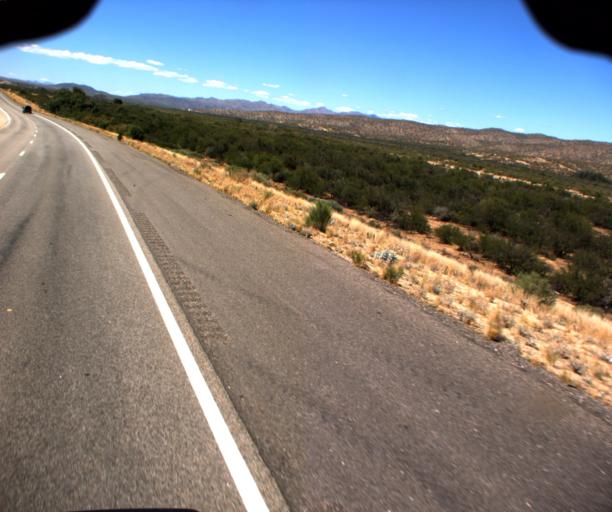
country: US
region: Arizona
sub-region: Yavapai County
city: Bagdad
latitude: 34.8210
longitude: -113.6263
